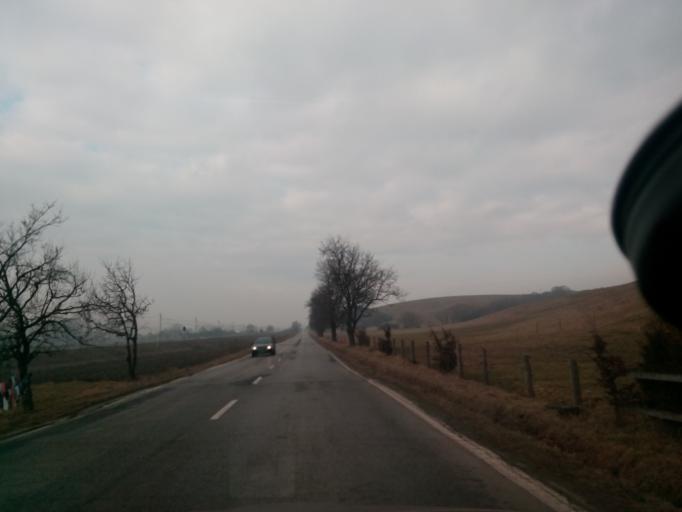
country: SK
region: Presovsky
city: Lipany
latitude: 49.1409
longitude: 21.0052
